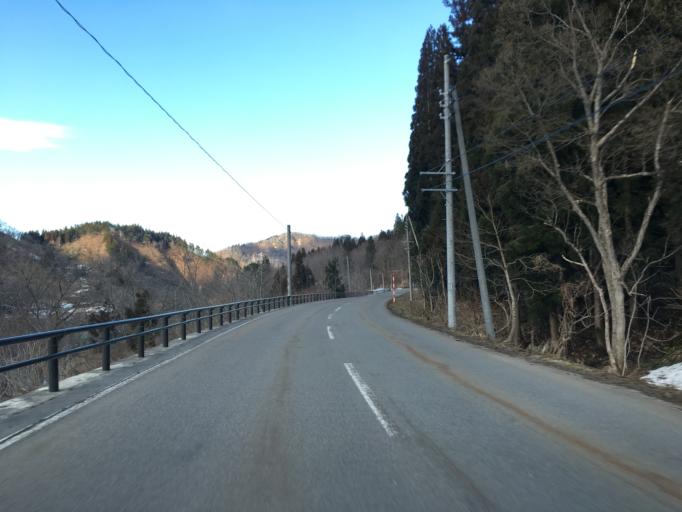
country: JP
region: Yamagata
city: Nagai
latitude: 37.9429
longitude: 139.9124
